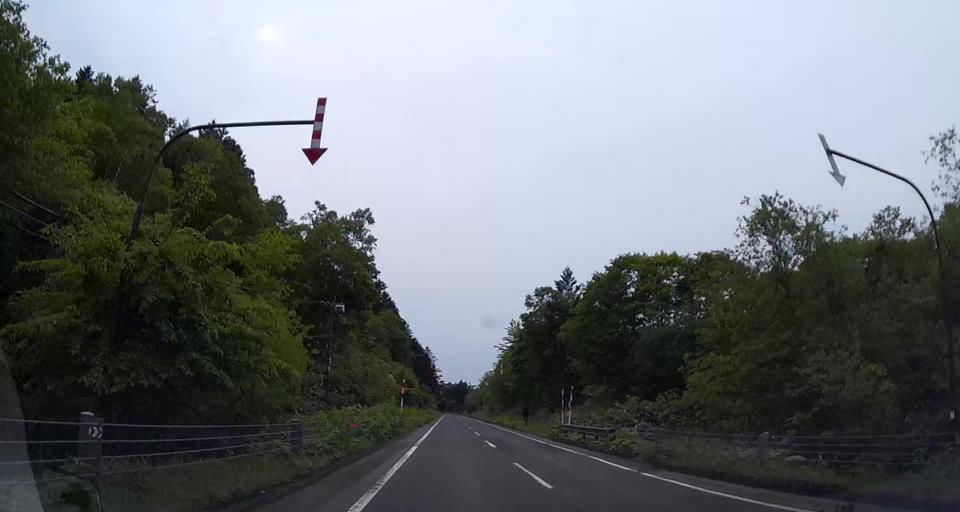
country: JP
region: Hokkaido
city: Shiraoi
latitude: 42.6490
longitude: 141.2076
